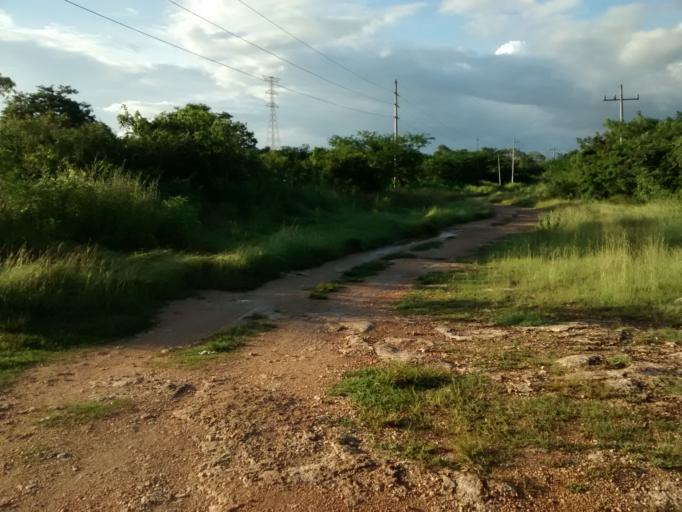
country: MX
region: Yucatan
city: Valladolid
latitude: 20.7047
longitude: -88.2057
